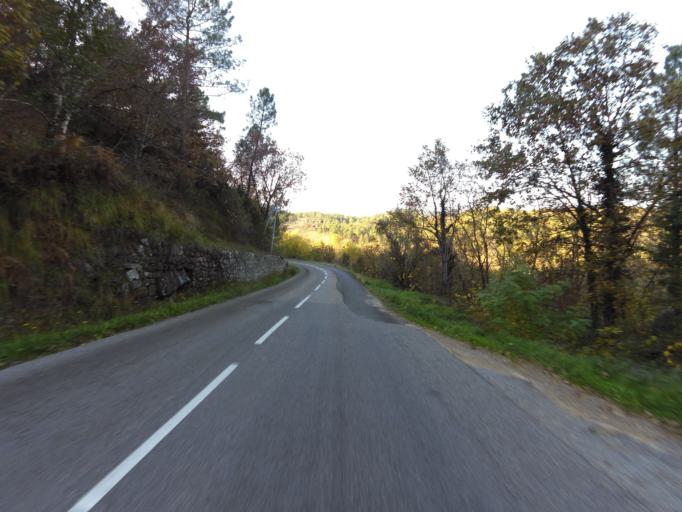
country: FR
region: Rhone-Alpes
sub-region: Departement de l'Ardeche
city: Joyeuse
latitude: 44.4964
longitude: 4.2177
